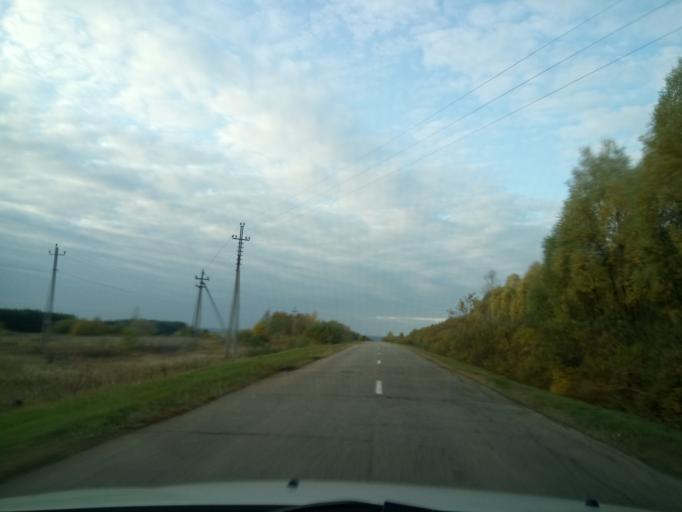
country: RU
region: Nizjnij Novgorod
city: Buturlino
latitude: 55.4973
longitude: 44.9992
